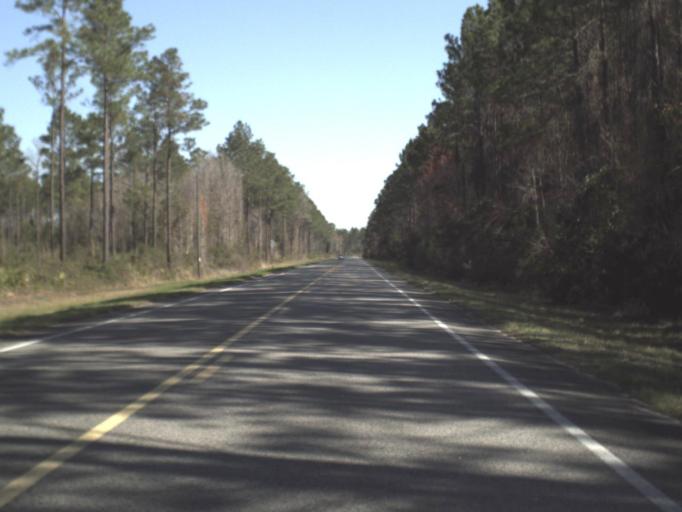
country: US
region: Florida
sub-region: Leon County
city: Woodville
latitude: 30.3295
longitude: -84.0278
